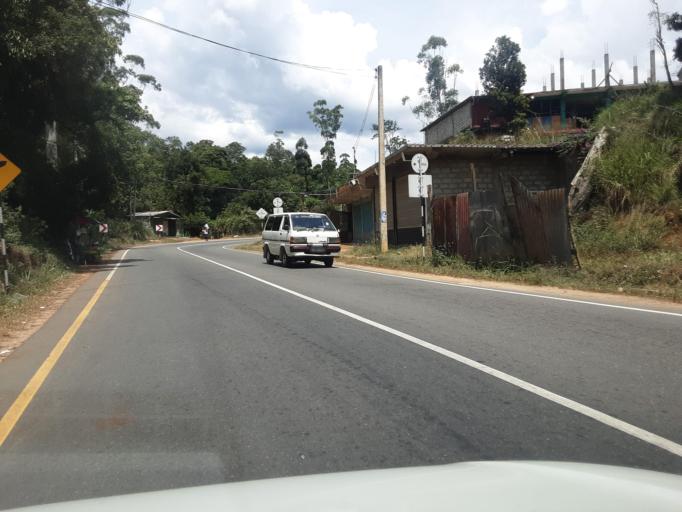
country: LK
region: Central
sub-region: Nuwara Eliya District
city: Nuwara Eliya
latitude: 6.9241
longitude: 80.8993
